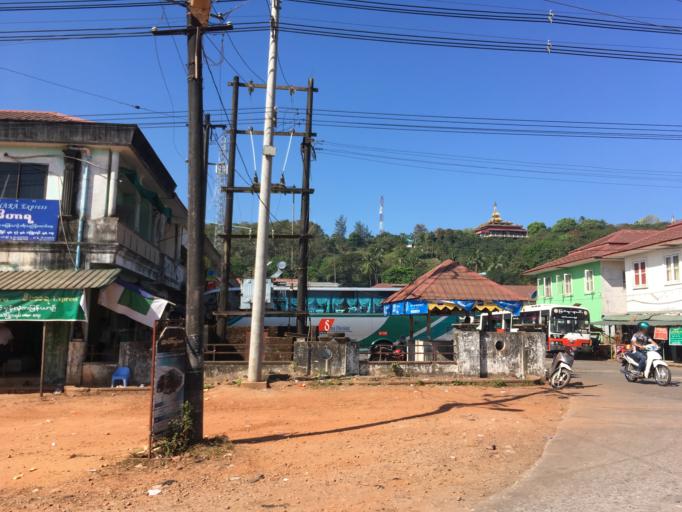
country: MM
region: Mon
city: Mawlamyine
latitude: 16.4776
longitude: 97.6332
